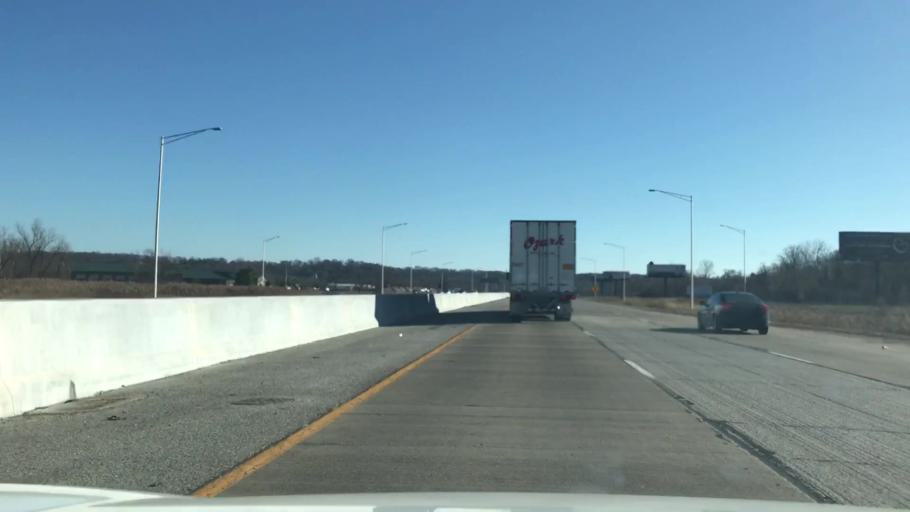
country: US
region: Illinois
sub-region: Saint Clair County
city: Alorton
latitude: 38.5816
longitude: -90.1069
